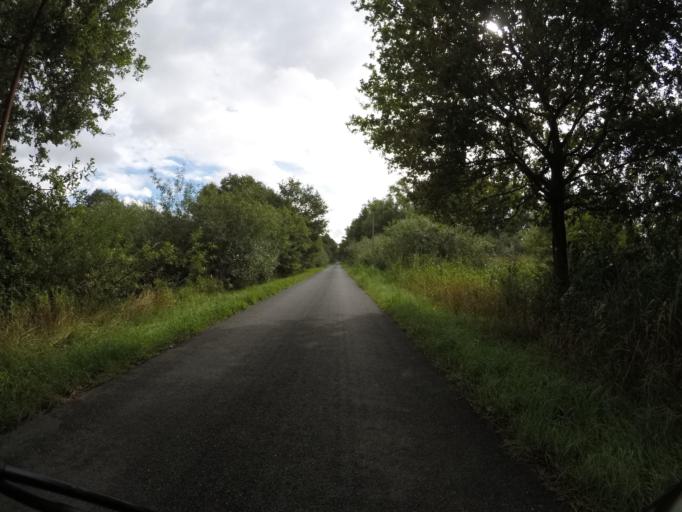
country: DE
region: Lower Saxony
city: Neu Darchau
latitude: 53.2626
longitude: 10.8500
